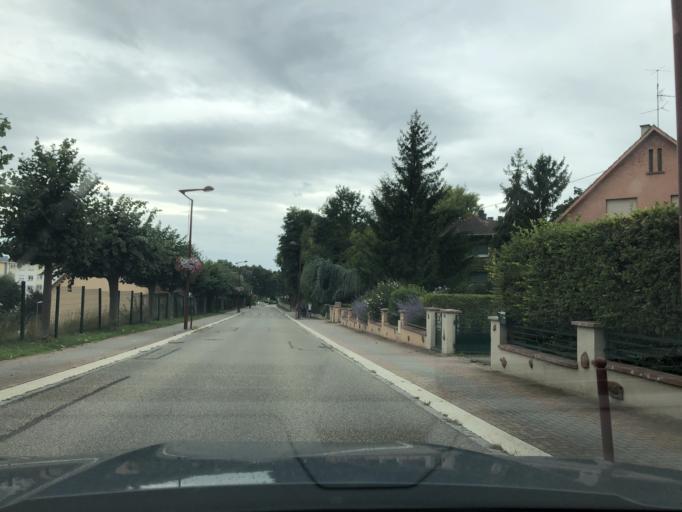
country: DE
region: Rheinland-Pfalz
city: Berg
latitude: 48.9722
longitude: 8.1846
